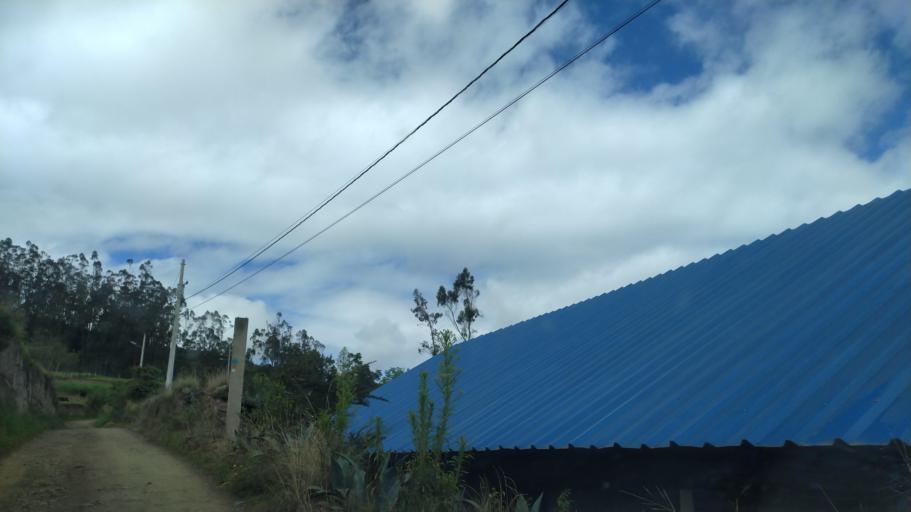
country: EC
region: Chimborazo
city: Riobamba
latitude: -1.6629
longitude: -78.5714
